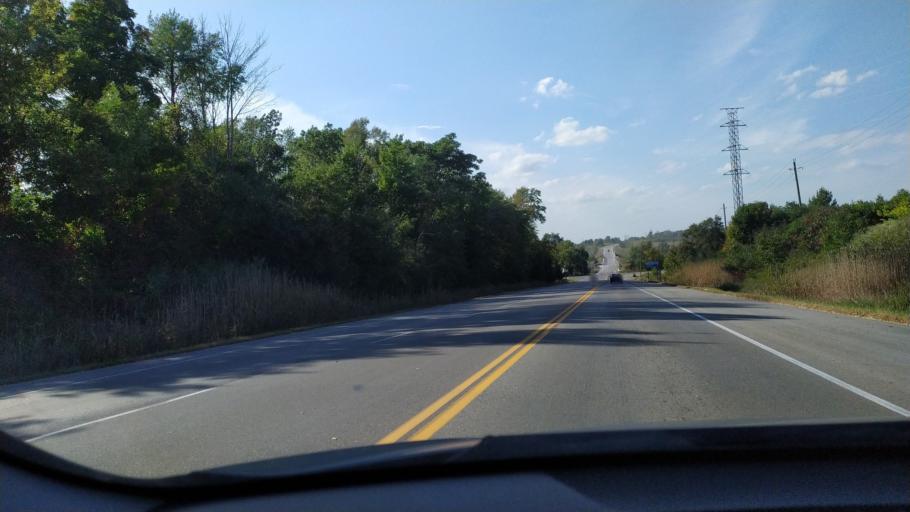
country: CA
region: Ontario
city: Ingersoll
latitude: 43.0676
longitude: -80.8457
